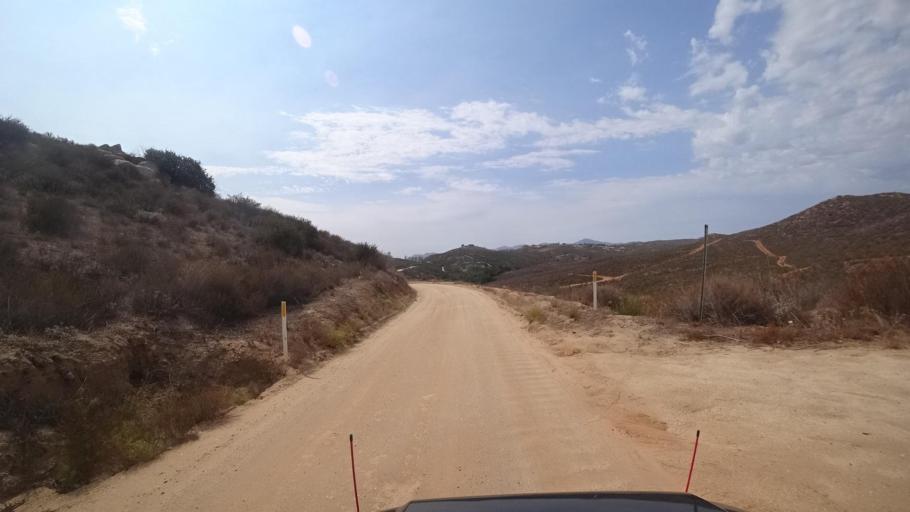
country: US
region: California
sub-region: San Diego County
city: Ramona
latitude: 33.1067
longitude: -116.8235
